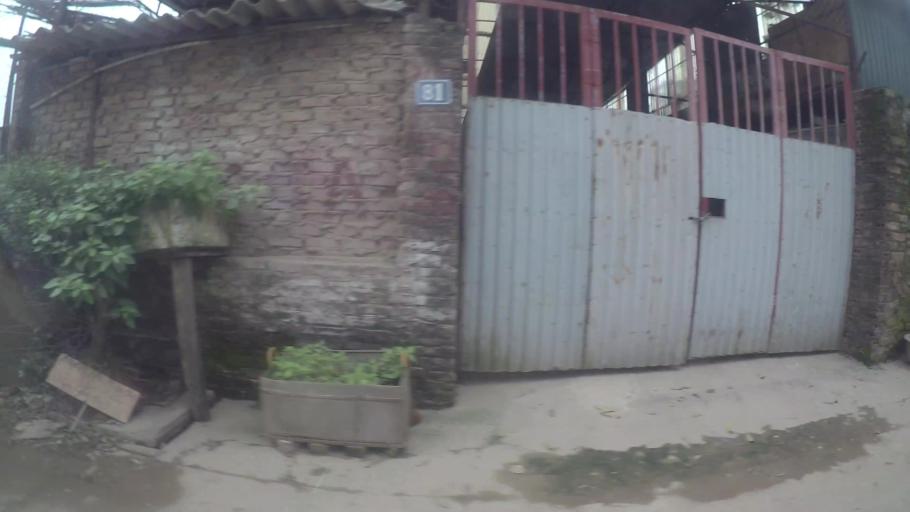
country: VN
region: Ha Noi
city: Tay Ho
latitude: 21.0673
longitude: 105.8352
